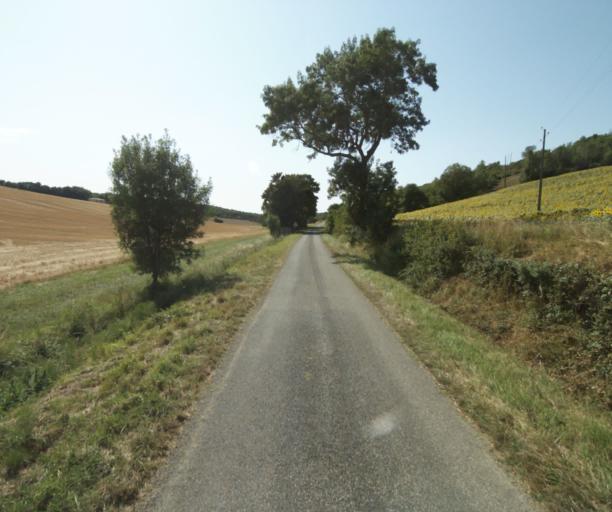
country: FR
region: Midi-Pyrenees
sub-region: Departement de la Haute-Garonne
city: Saint-Felix-Lauragais
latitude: 43.4371
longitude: 1.8414
